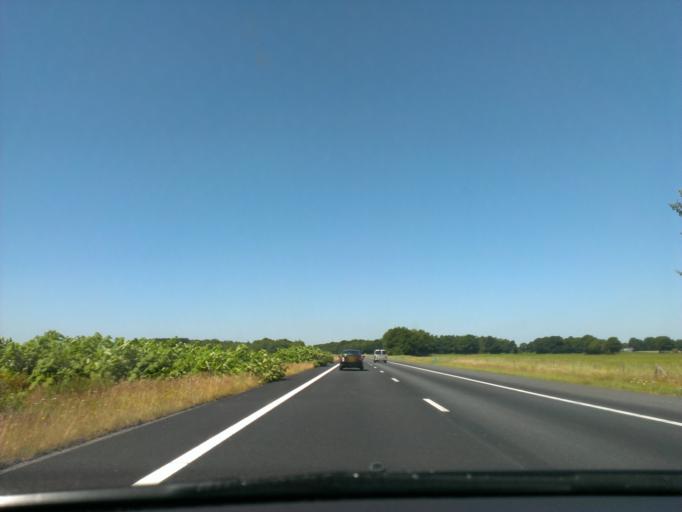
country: NL
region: Drenthe
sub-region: Gemeente Coevorden
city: Dalen
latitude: 52.7237
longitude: 6.7078
